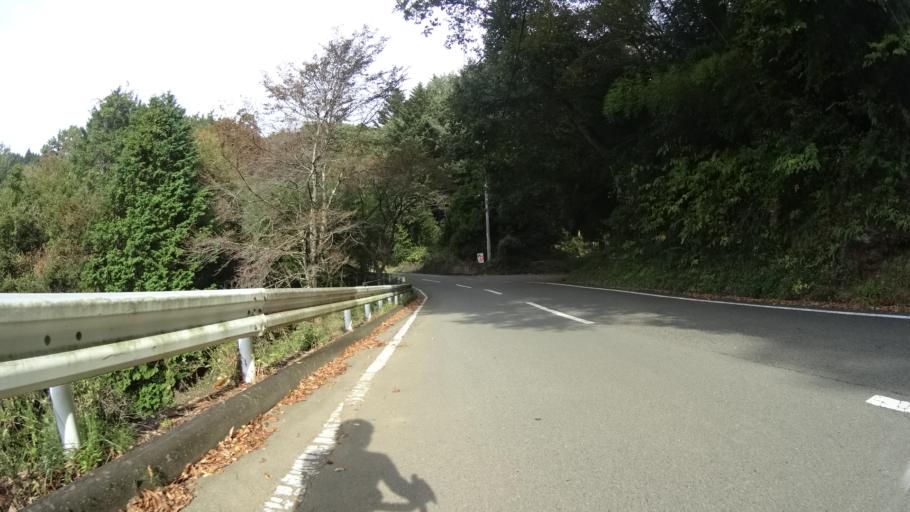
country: JP
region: Yamanashi
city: Uenohara
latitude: 35.6262
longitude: 139.0315
